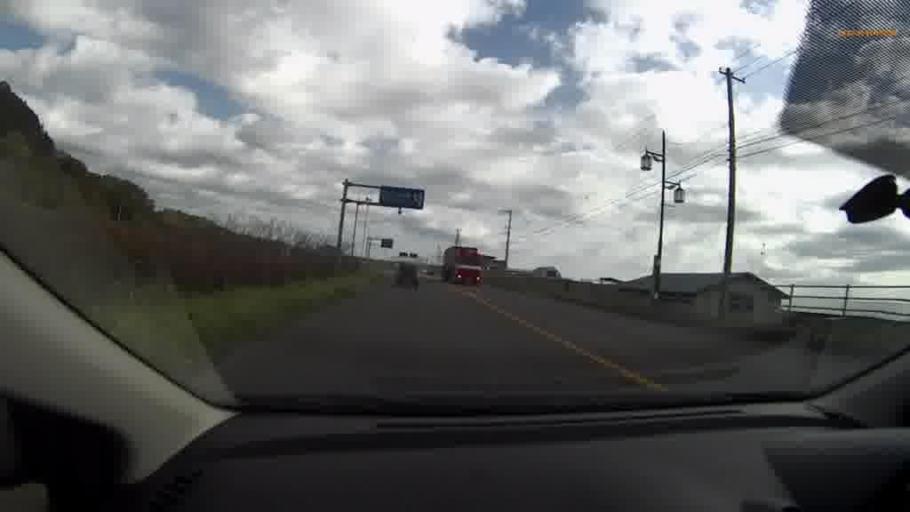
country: JP
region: Hokkaido
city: Kushiro
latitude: 42.9631
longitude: 144.1134
